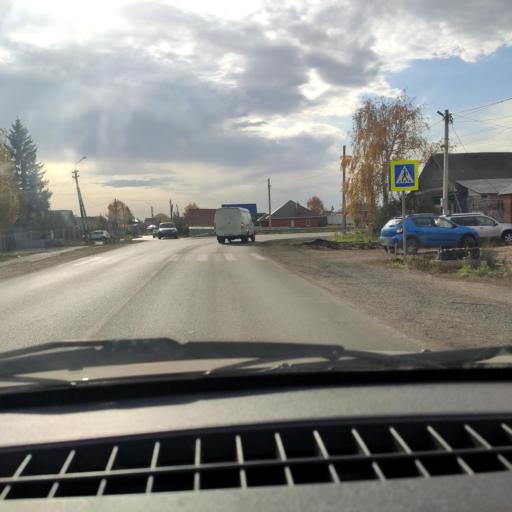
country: RU
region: Bashkortostan
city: Ufa
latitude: 54.6118
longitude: 55.9007
